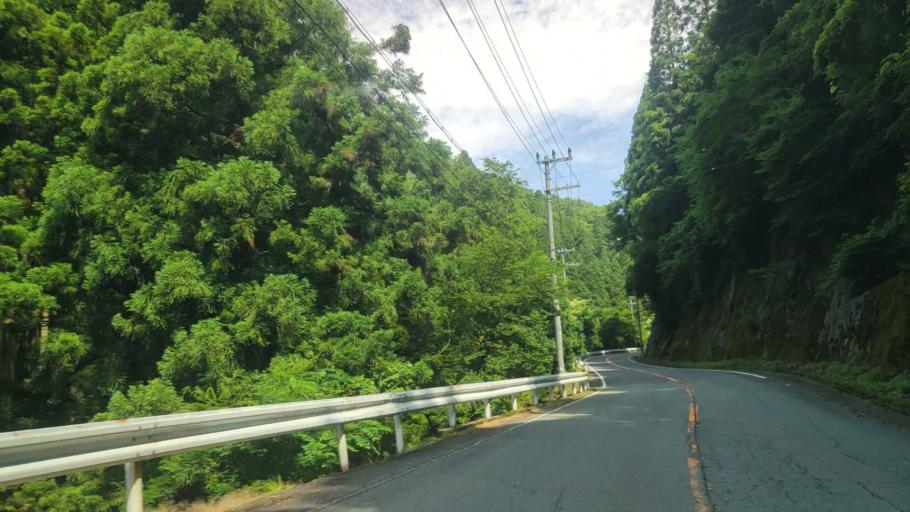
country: JP
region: Hyogo
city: Toyooka
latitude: 35.6318
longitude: 134.7814
